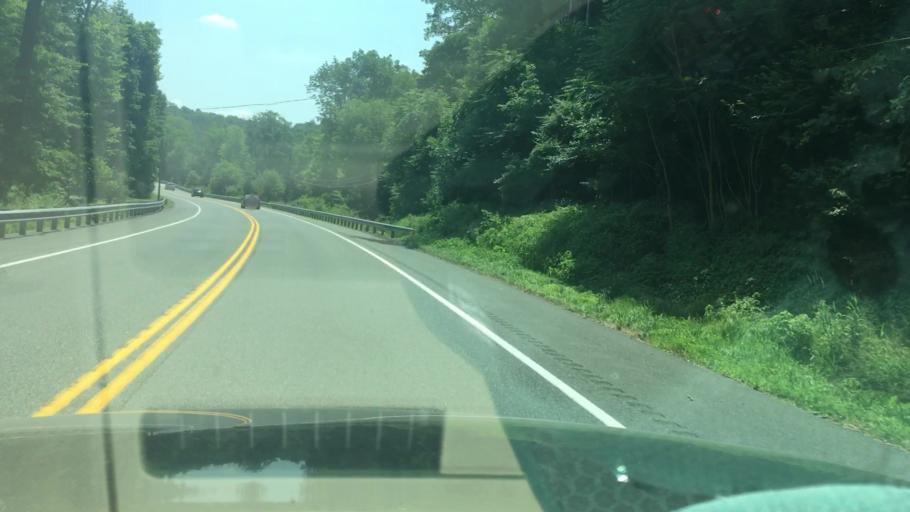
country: US
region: Pennsylvania
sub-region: Lehigh County
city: Schnecksville
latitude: 40.6740
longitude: -75.6916
